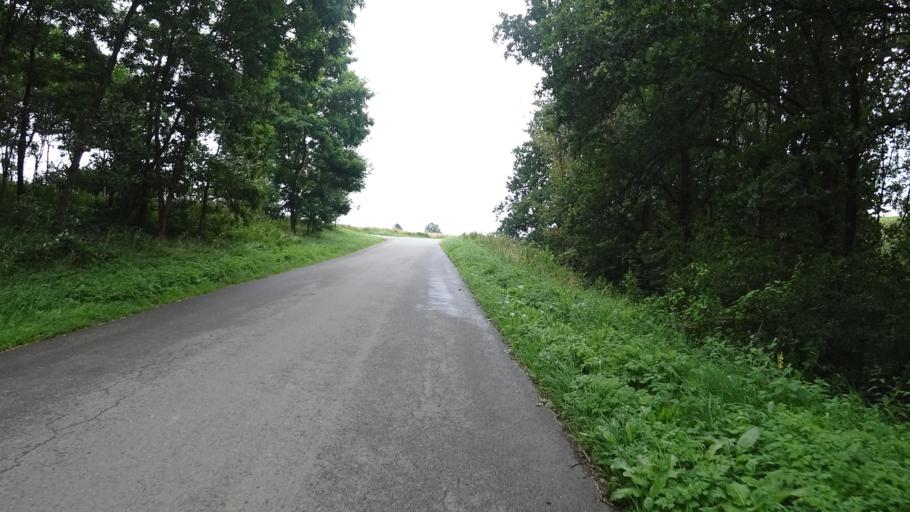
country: BE
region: Wallonia
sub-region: Province du Luxembourg
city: Chiny
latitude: 49.8006
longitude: 5.3742
